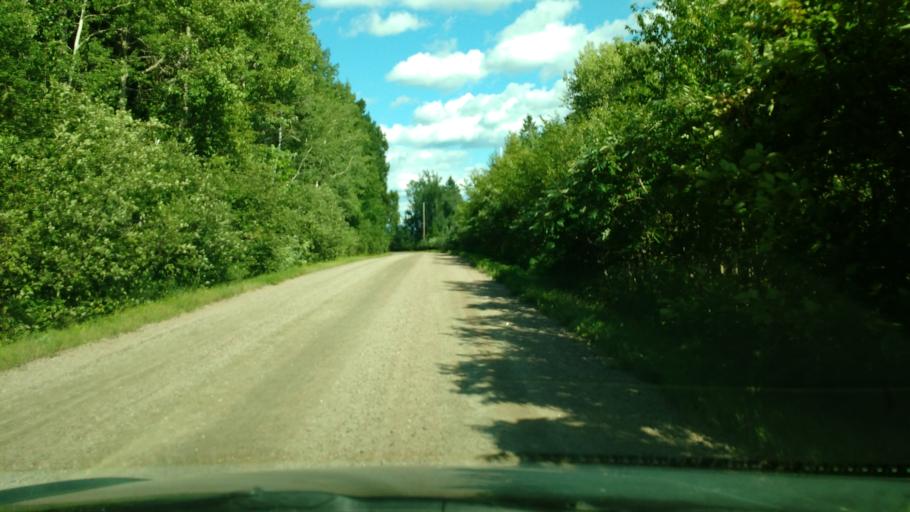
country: CA
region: Ontario
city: Powassan
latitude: 46.1896
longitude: -79.2853
